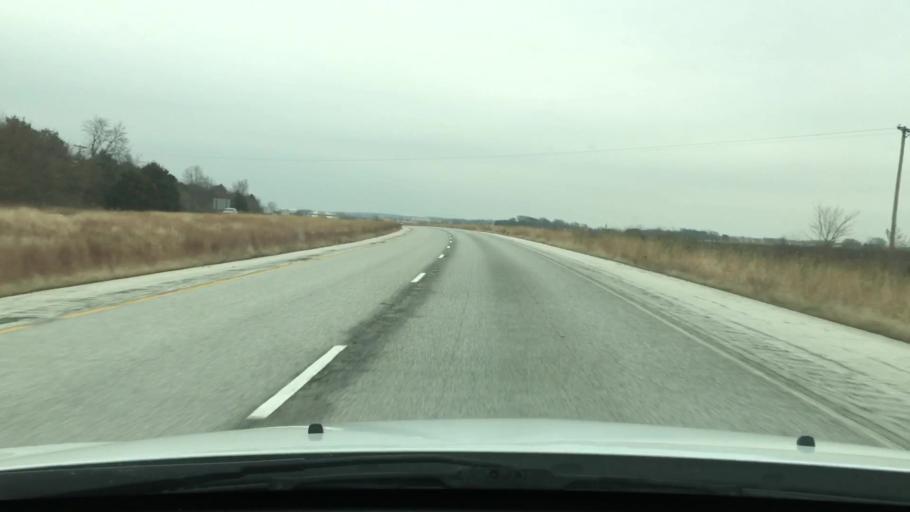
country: US
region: Illinois
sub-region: Morgan County
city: South Jacksonville
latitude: 39.6897
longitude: -90.2014
